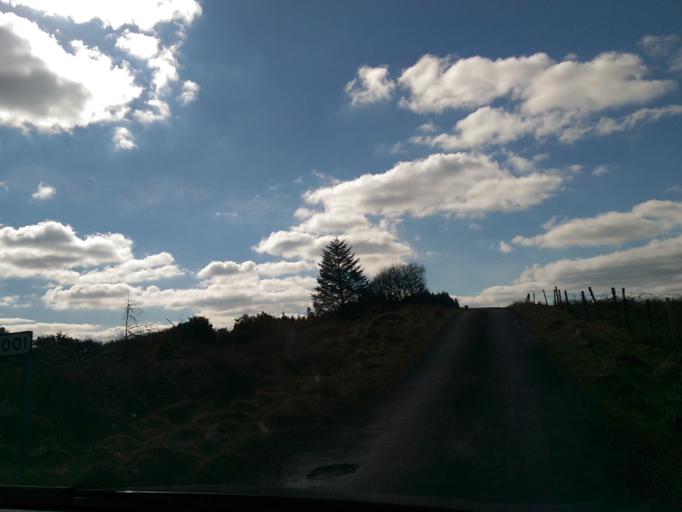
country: IE
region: Leinster
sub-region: Laois
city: Mountrath
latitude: 53.0908
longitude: -7.6235
